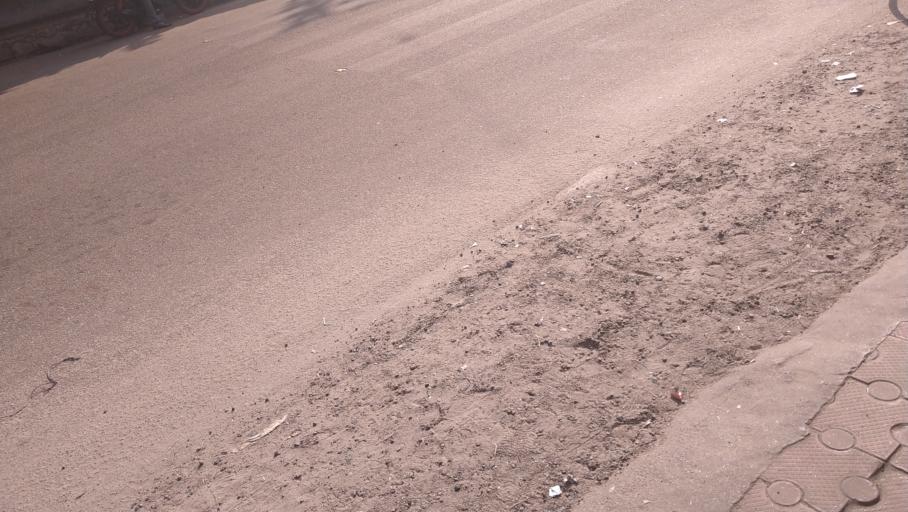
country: IN
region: Kerala
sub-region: Ernakulam
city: Angamali
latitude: 10.1880
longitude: 76.3285
